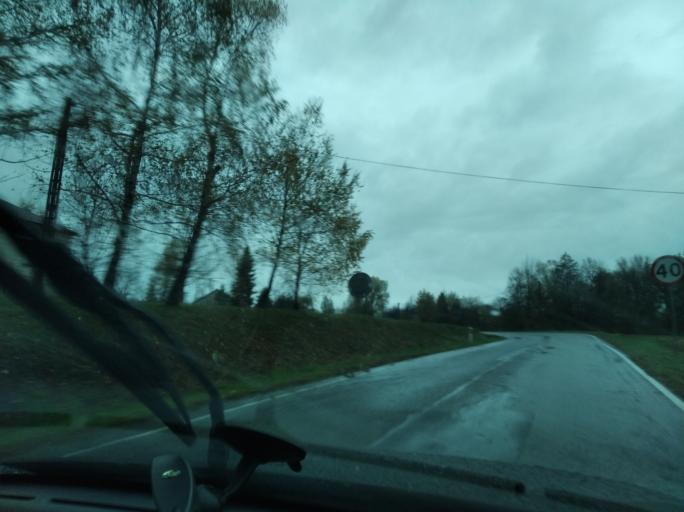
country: PL
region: Subcarpathian Voivodeship
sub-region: Powiat lancucki
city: Handzlowka
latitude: 49.9845
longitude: 22.1921
